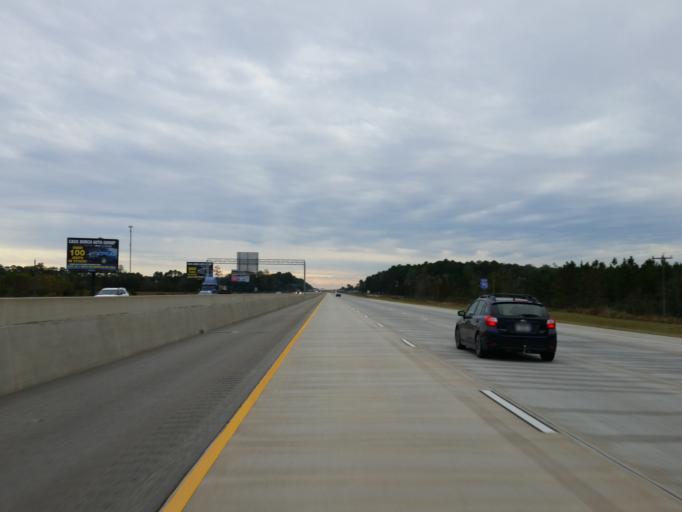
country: US
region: Georgia
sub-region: Cook County
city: Sparks
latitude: 31.2530
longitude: -83.4685
